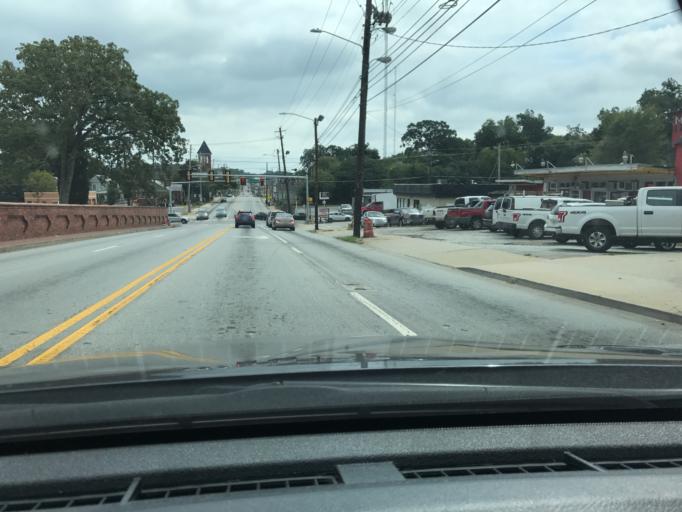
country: US
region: Georgia
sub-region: Fulton County
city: Atlanta
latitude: 33.7467
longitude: -84.3692
